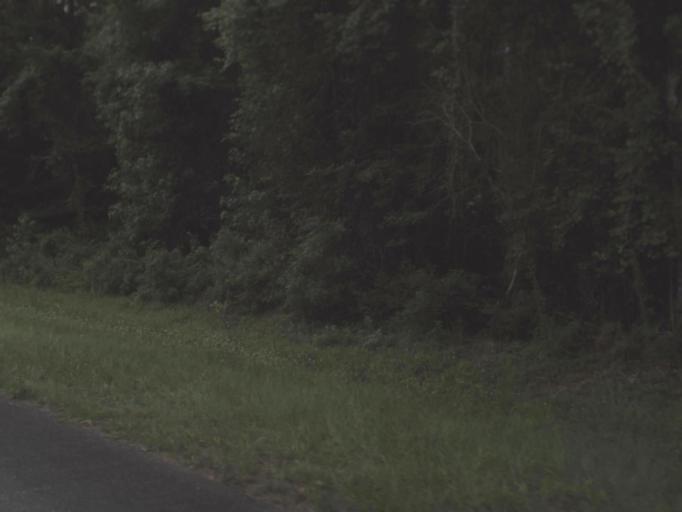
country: US
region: Florida
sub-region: Union County
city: Lake Butler
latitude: 30.1001
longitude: -82.4803
